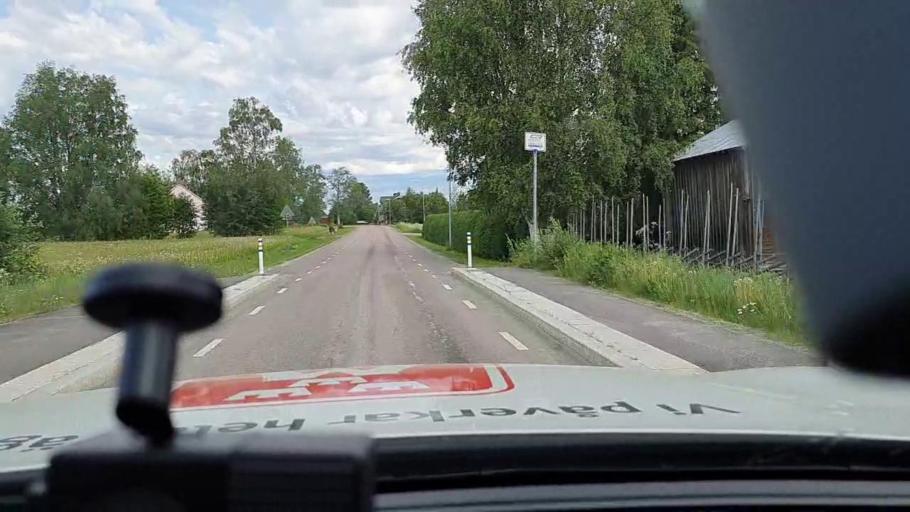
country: SE
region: Norrbotten
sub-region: Bodens Kommun
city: Saevast
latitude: 65.6825
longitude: 21.7996
